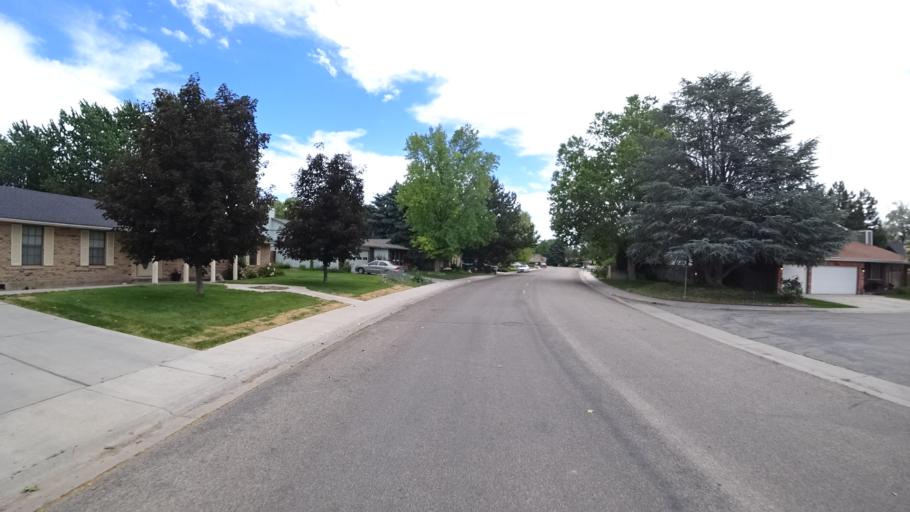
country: US
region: Idaho
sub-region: Ada County
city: Eagle
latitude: 43.6419
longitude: -116.3324
